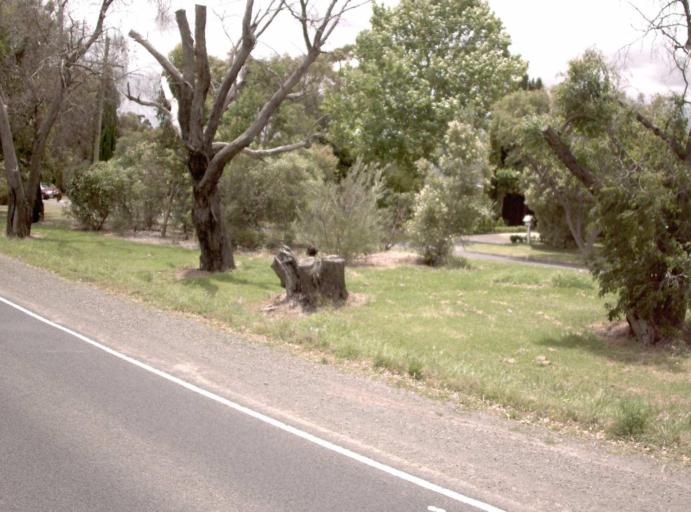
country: AU
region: Victoria
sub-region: Yarra Ranges
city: Lilydale
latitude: -37.7313
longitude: 145.3772
